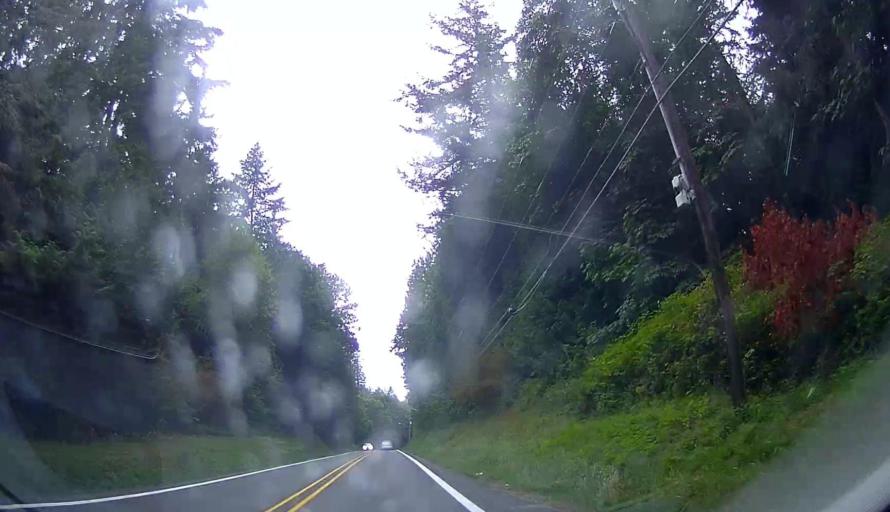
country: US
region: Washington
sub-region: Snohomish County
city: Warm Beach
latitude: 48.1221
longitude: -122.3537
